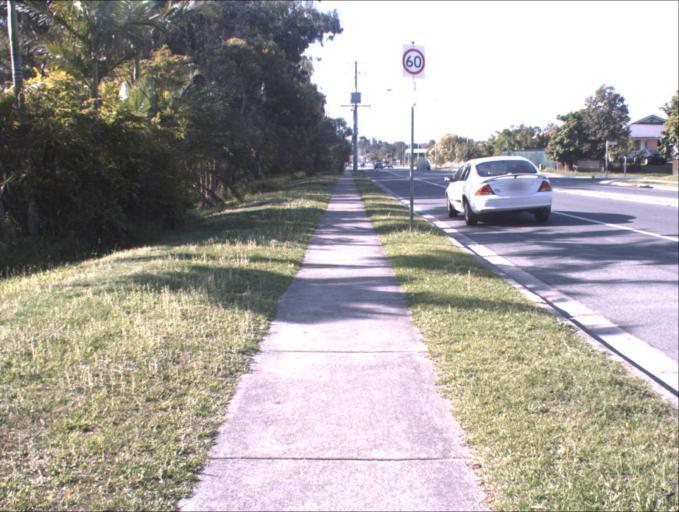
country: AU
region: Queensland
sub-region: Logan
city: Logan Reserve
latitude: -27.6795
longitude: 153.0889
